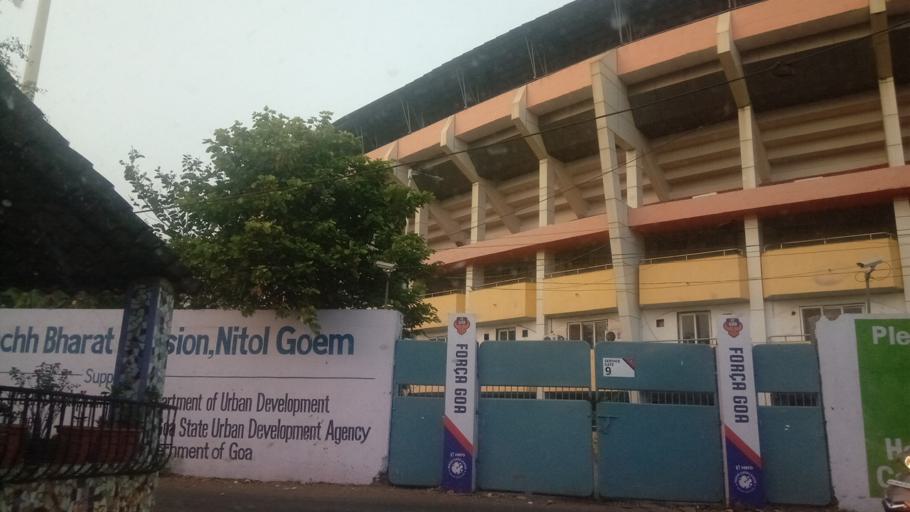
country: IN
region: Goa
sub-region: South Goa
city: Madgaon
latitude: 15.2881
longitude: 73.9618
